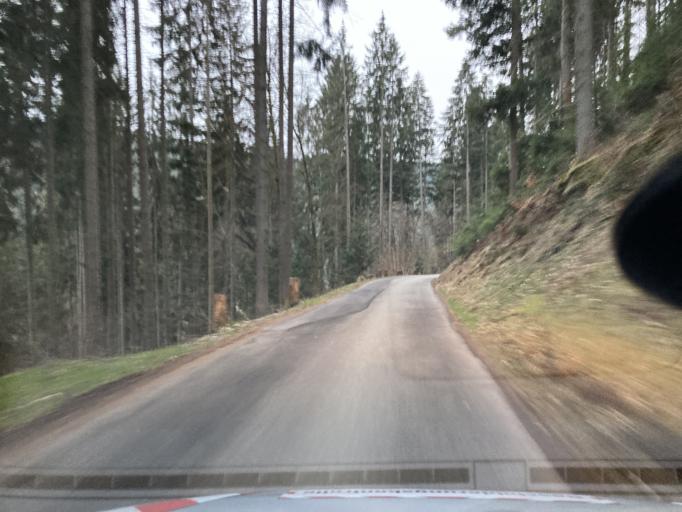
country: DE
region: Baden-Wuerttemberg
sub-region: Karlsruhe Region
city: Neubulach
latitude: 48.6628
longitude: 8.6552
